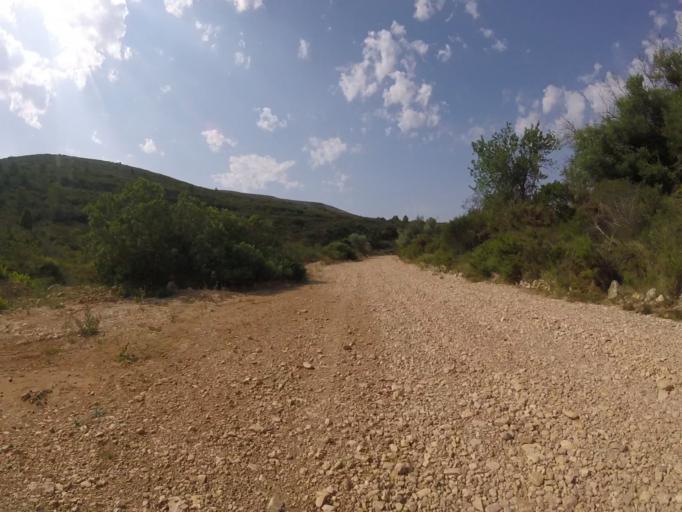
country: ES
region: Valencia
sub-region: Provincia de Castello
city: Alcala de Xivert
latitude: 40.3299
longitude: 0.1938
